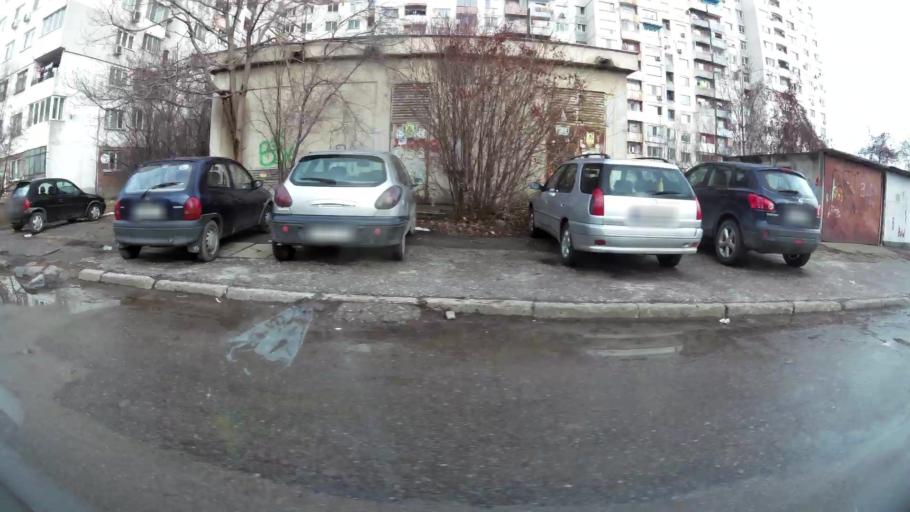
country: BG
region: Sofiya
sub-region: Obshtina Bozhurishte
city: Bozhurishte
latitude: 42.7230
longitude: 23.2464
